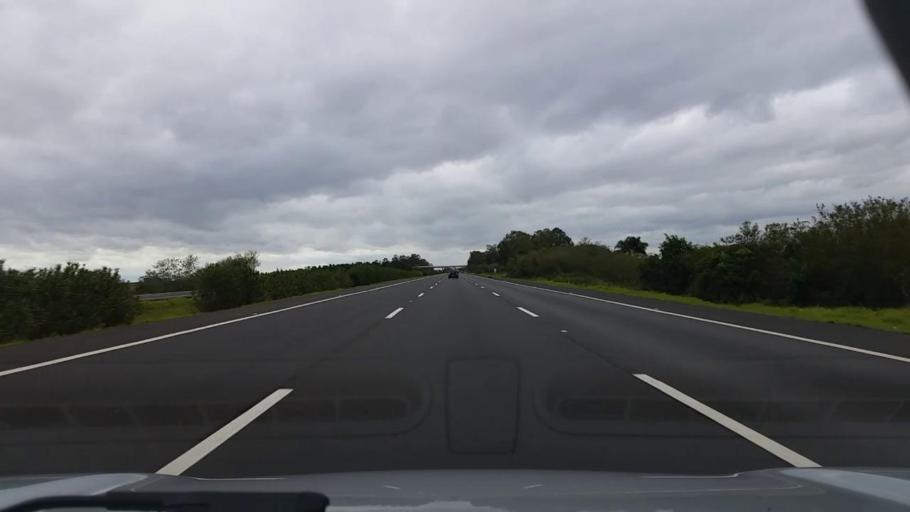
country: BR
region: Rio Grande do Sul
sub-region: Rolante
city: Rolante
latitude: -29.8843
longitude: -50.5705
